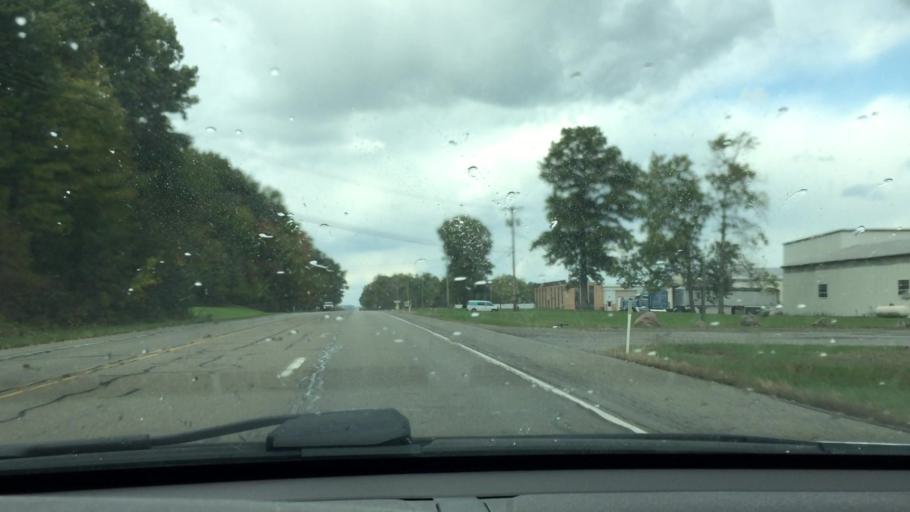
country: US
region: Pennsylvania
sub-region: Lawrence County
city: Oakwood
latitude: 41.0598
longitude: -80.4516
